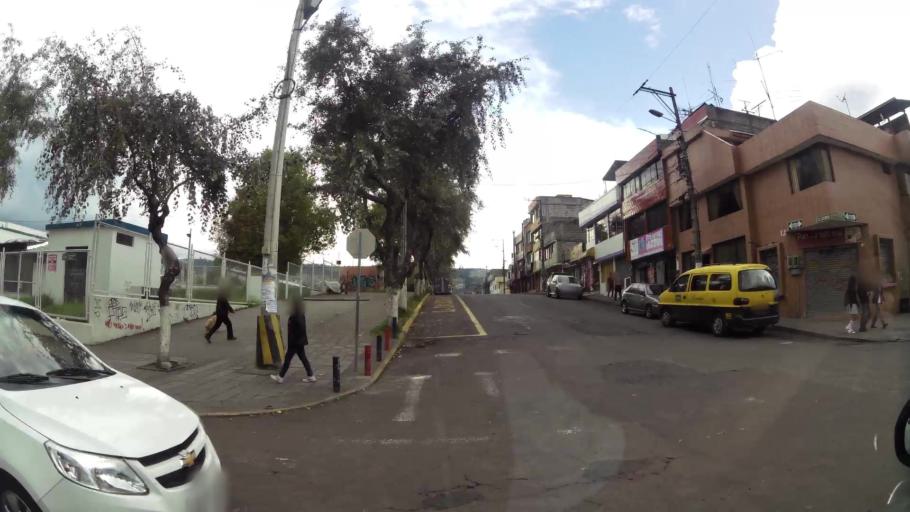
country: EC
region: Pichincha
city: Quito
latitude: -0.2686
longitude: -78.5401
